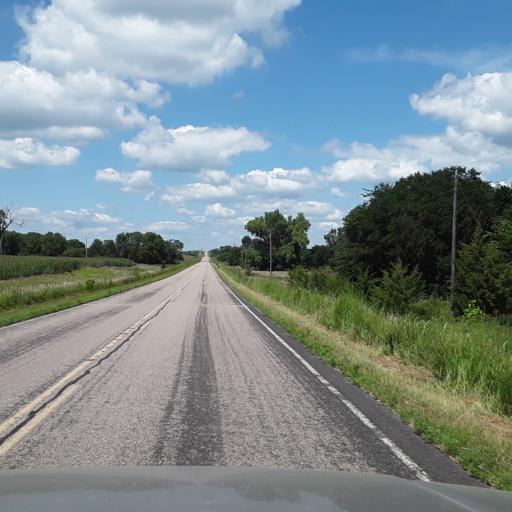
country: US
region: Nebraska
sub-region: Nance County
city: Genoa
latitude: 41.5007
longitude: -97.6959
